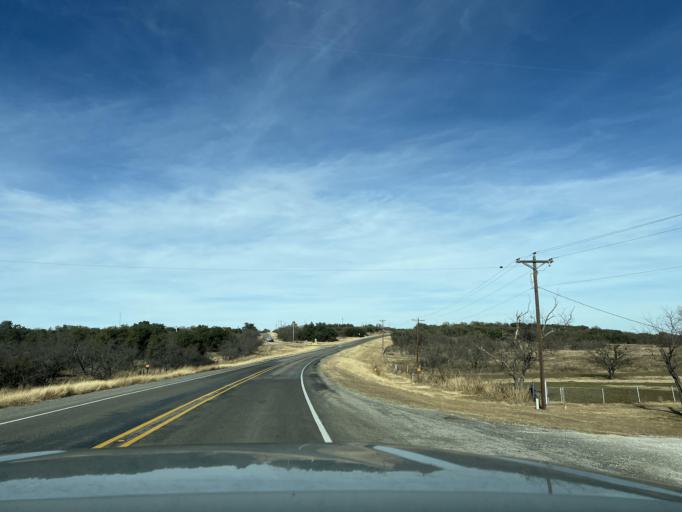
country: US
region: Texas
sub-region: Eastland County
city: Cisco
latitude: 32.4240
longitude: -98.9871
